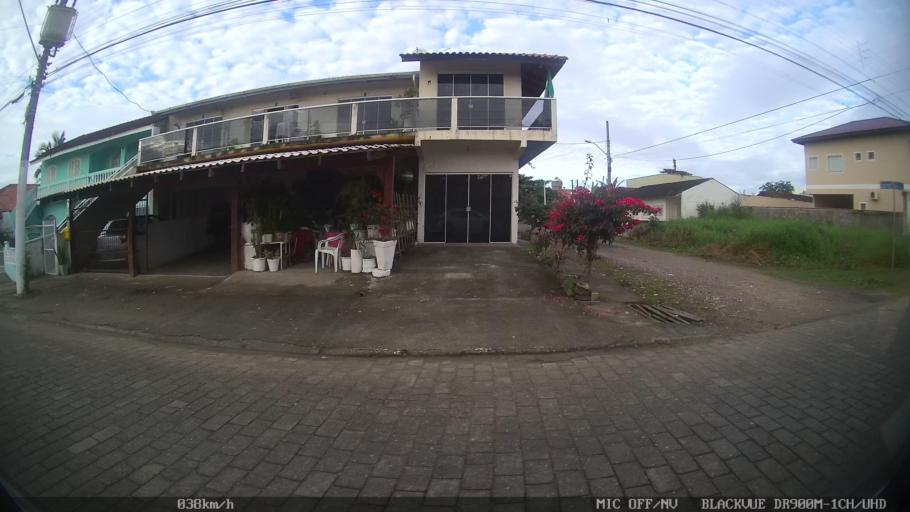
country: BR
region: Santa Catarina
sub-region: Barra Velha
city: Barra Velha
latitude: -26.6297
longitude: -48.6901
